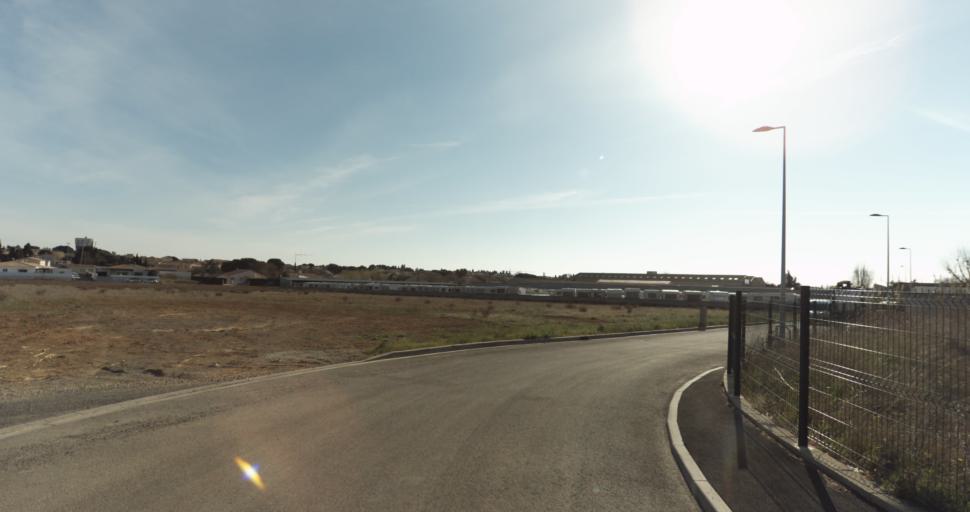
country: FR
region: Languedoc-Roussillon
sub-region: Departement de l'Herault
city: Marseillan
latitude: 43.3596
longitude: 3.5204
